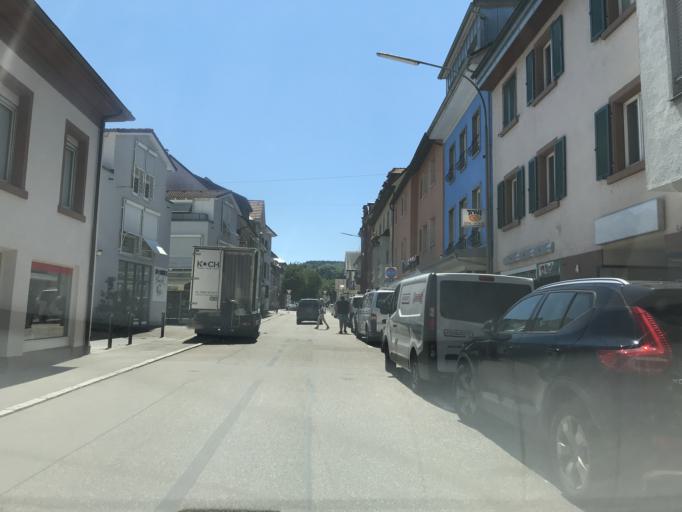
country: DE
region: Baden-Wuerttemberg
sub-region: Freiburg Region
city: Schopfheim
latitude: 47.6499
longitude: 7.8230
